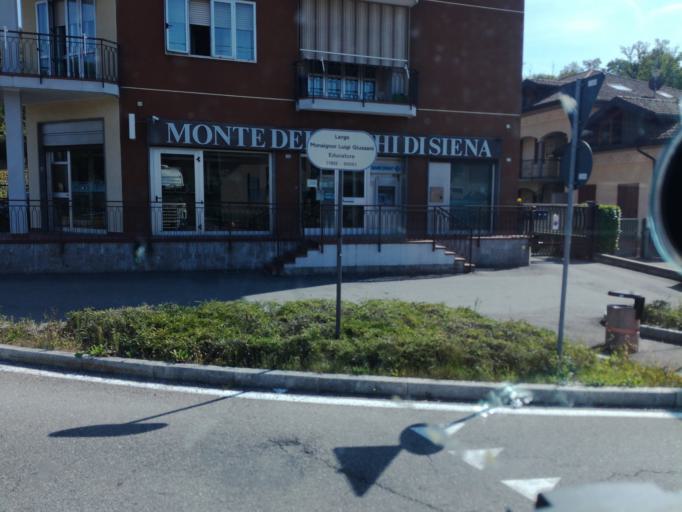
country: IT
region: Lombardy
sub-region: Provincia di Varese
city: Castronno
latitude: 45.7557
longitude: 8.8108
